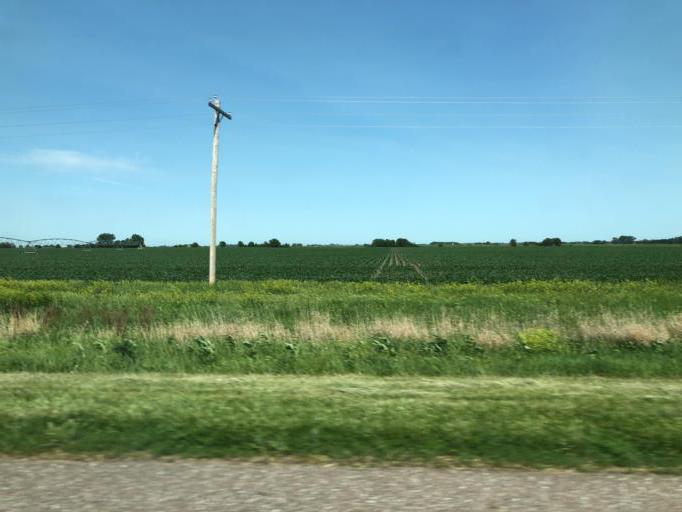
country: US
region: Nebraska
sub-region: Fillmore County
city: Geneva
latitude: 40.6125
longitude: -97.5957
